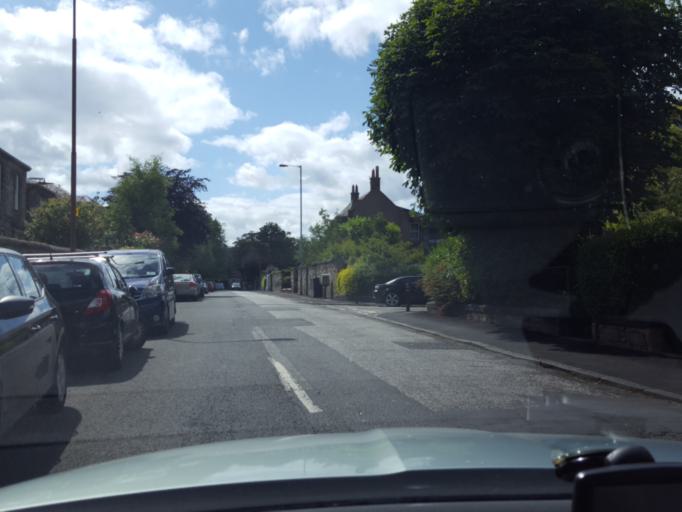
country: GB
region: Scotland
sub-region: Edinburgh
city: Edinburgh
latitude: 55.9784
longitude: -3.1937
